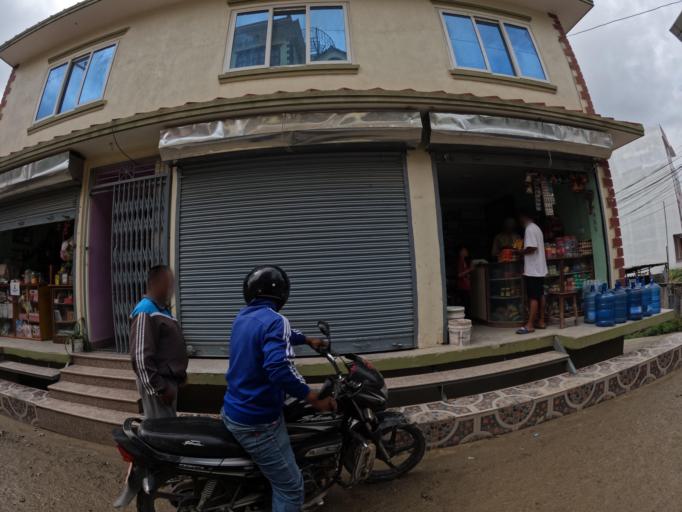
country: NP
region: Central Region
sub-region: Bagmati Zone
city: Kathmandu
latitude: 27.7479
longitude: 85.3193
